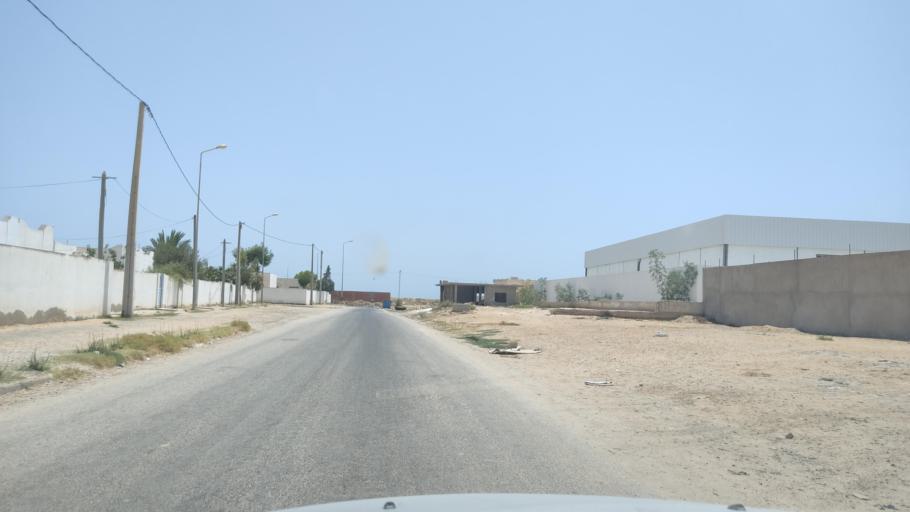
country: TN
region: Safaqis
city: Sfax
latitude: 34.6623
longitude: 10.7020
